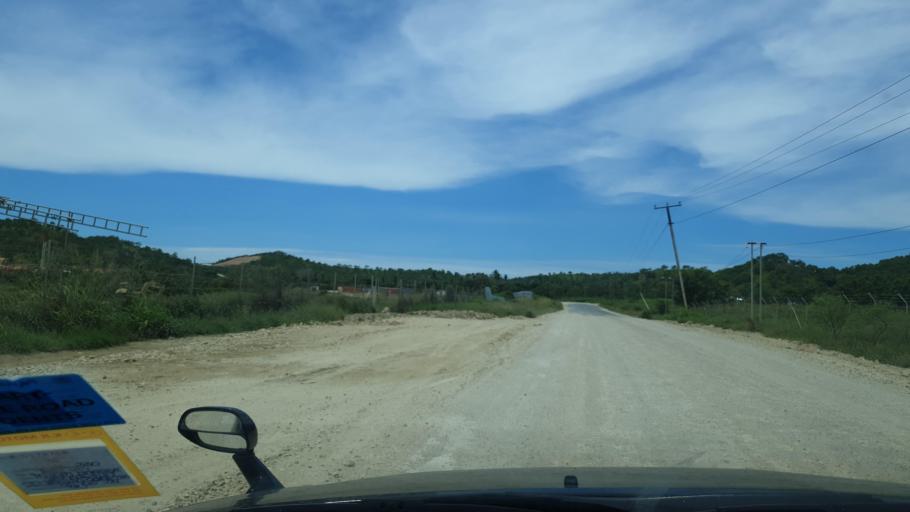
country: PG
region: National Capital
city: Port Moresby
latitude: -9.4217
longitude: 147.0761
